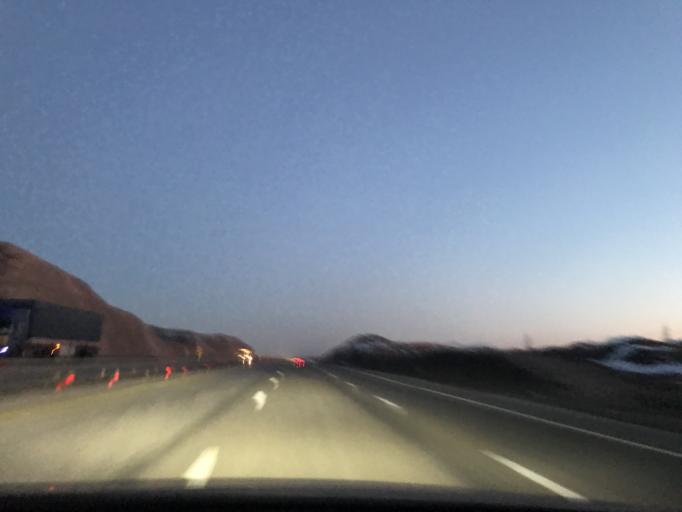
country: IR
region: Isfahan
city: Kashan
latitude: 33.8105
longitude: 51.6438
